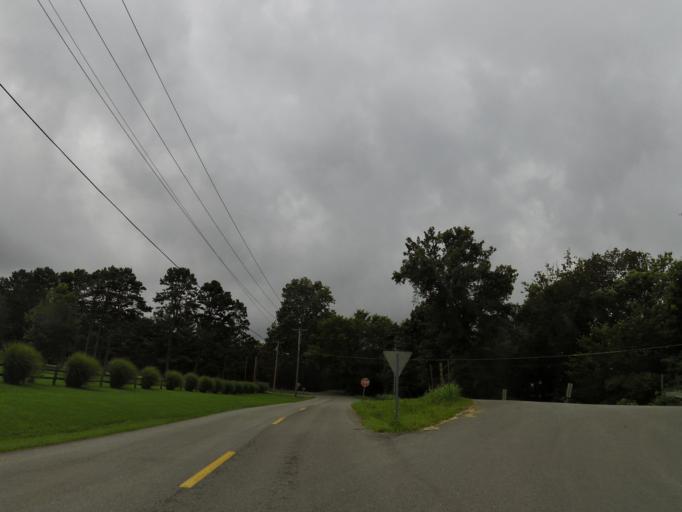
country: US
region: Missouri
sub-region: Cape Girardeau County
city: Cape Girardeau
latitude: 37.3589
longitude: -89.5632
